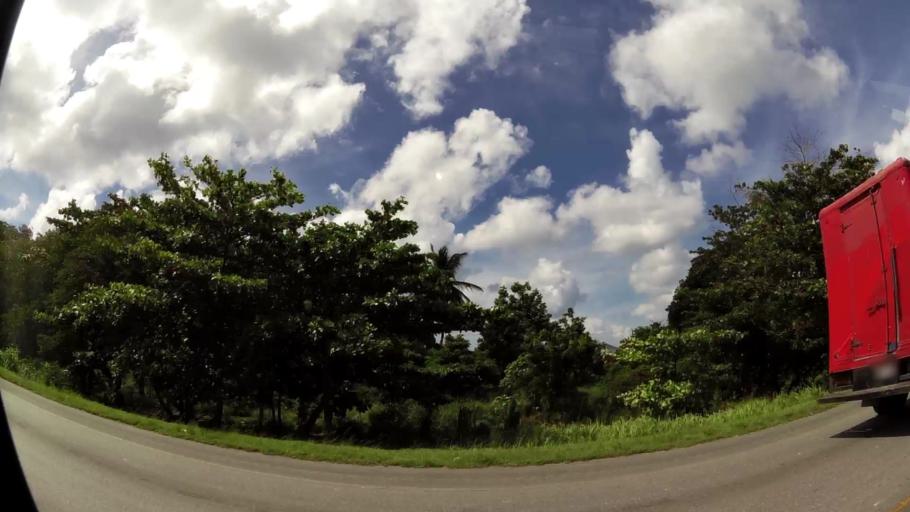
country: BB
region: Saint Michael
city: Bridgetown
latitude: 13.1185
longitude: -59.6269
